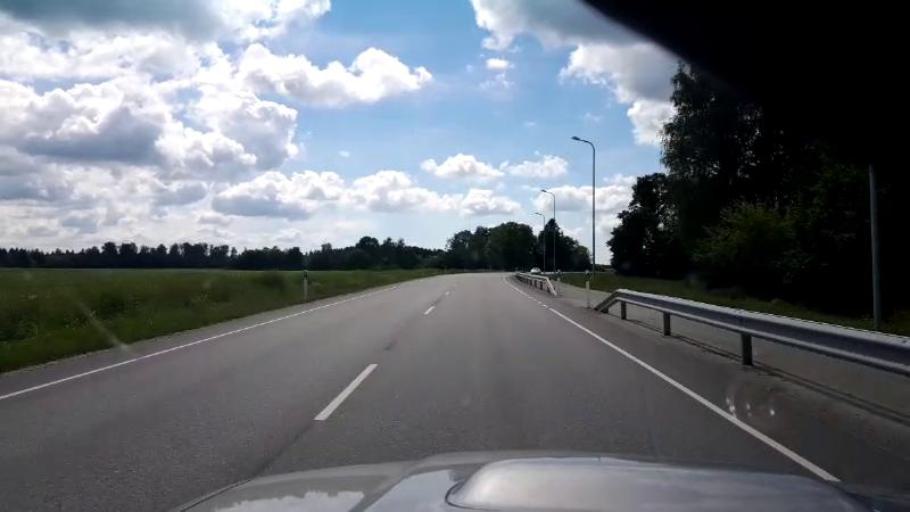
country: EE
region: Jaervamaa
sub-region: Jaerva-Jaani vald
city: Jarva-Jaani
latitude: 59.0240
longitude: 25.7050
